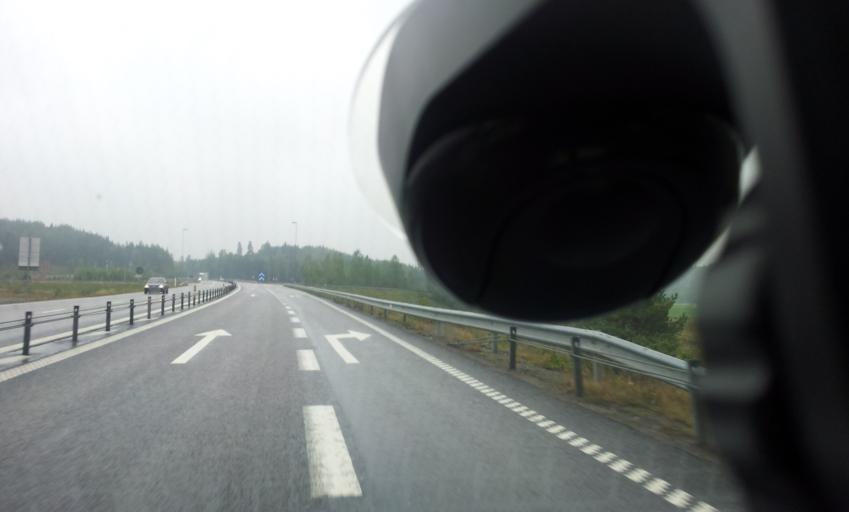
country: SE
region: OEstergoetland
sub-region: Valdemarsviks Kommun
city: Valdemarsvik
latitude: 58.2236
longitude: 16.5526
